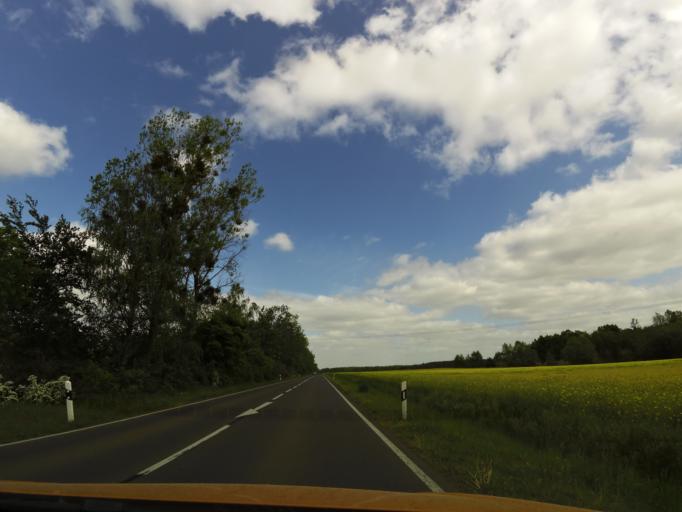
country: DE
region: Saxony-Anhalt
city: Mockern
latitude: 52.1972
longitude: 11.9021
